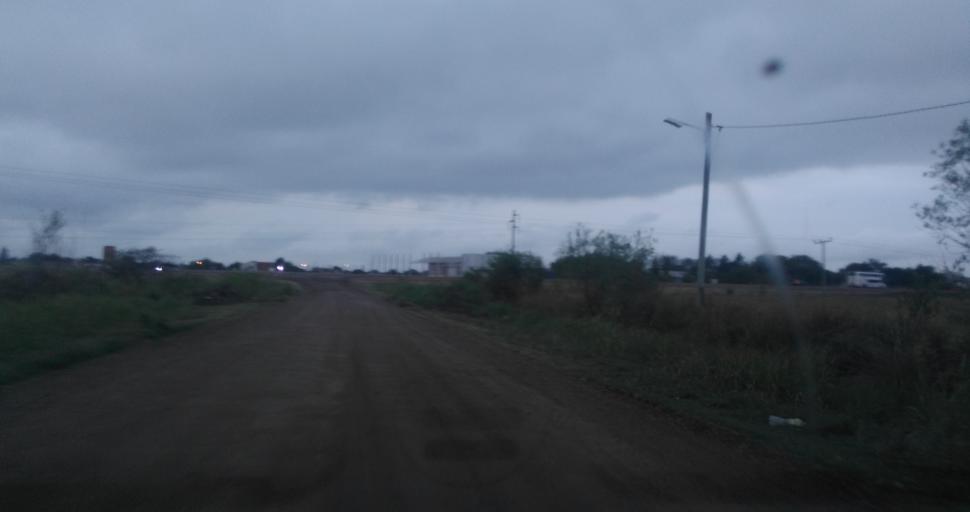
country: AR
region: Chaco
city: Fontana
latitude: -27.3961
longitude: -58.9972
